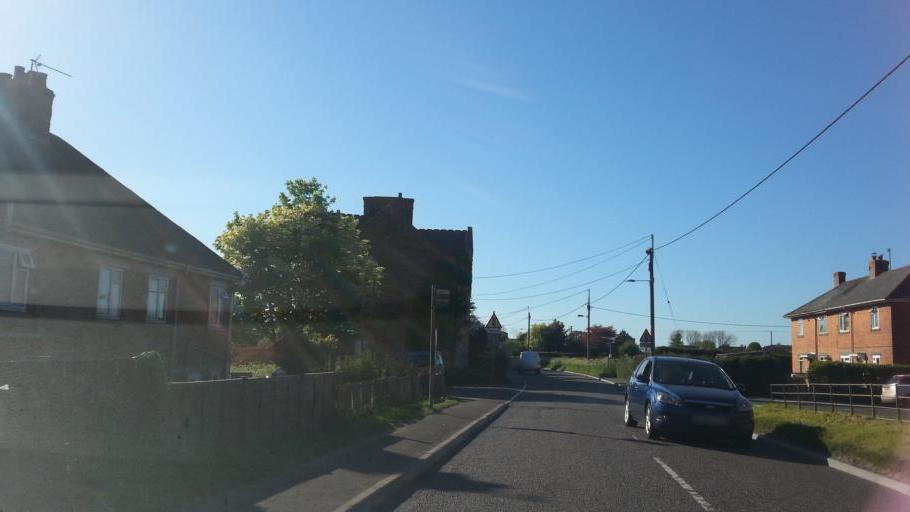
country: GB
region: England
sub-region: Somerset
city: Castle Cary
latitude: 51.0918
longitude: -2.5094
